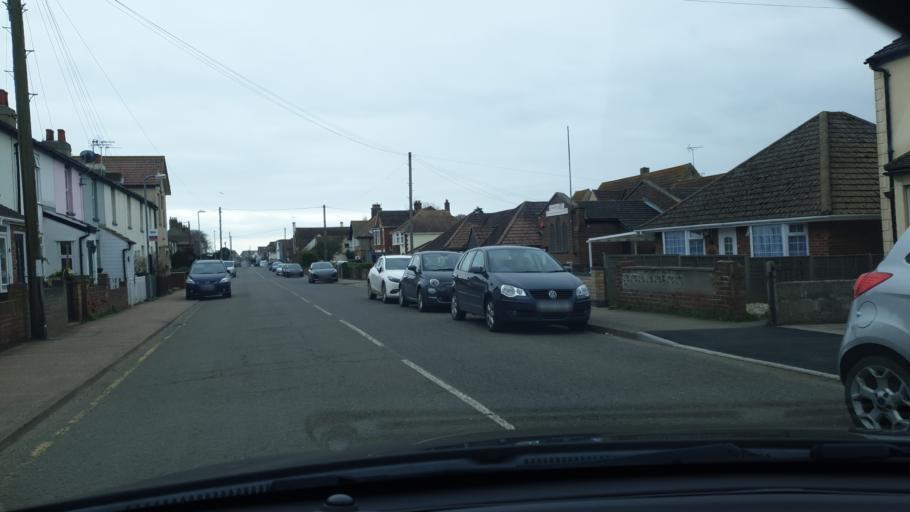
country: GB
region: England
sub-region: Essex
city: Walton-on-the-Naze
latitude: 51.8577
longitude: 1.2785
